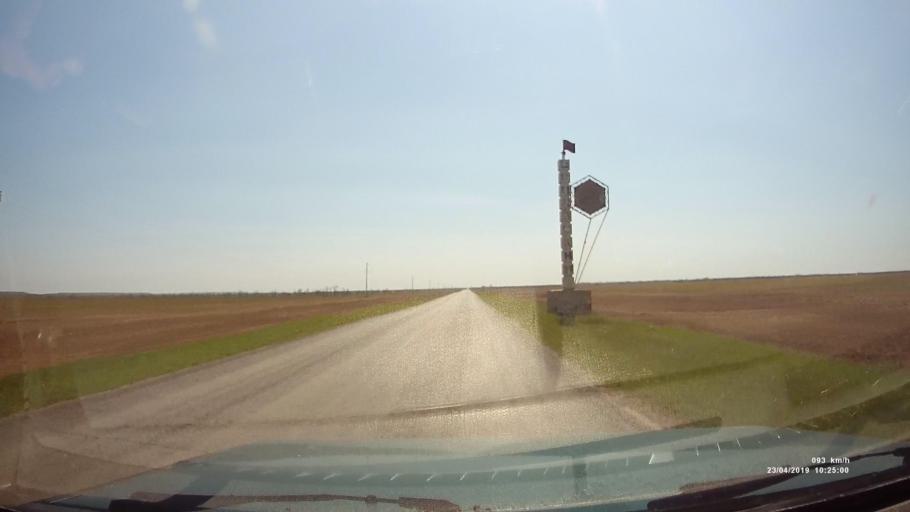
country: RU
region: Rostov
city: Sovetskoye
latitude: 46.6344
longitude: 42.4500
